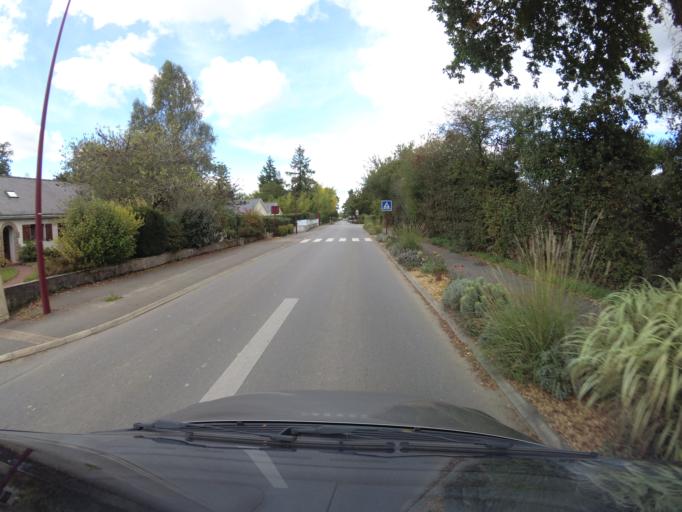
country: FR
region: Pays de la Loire
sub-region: Departement de la Loire-Atlantique
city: Suce-sur-Erdre
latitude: 47.3498
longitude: -1.5360
